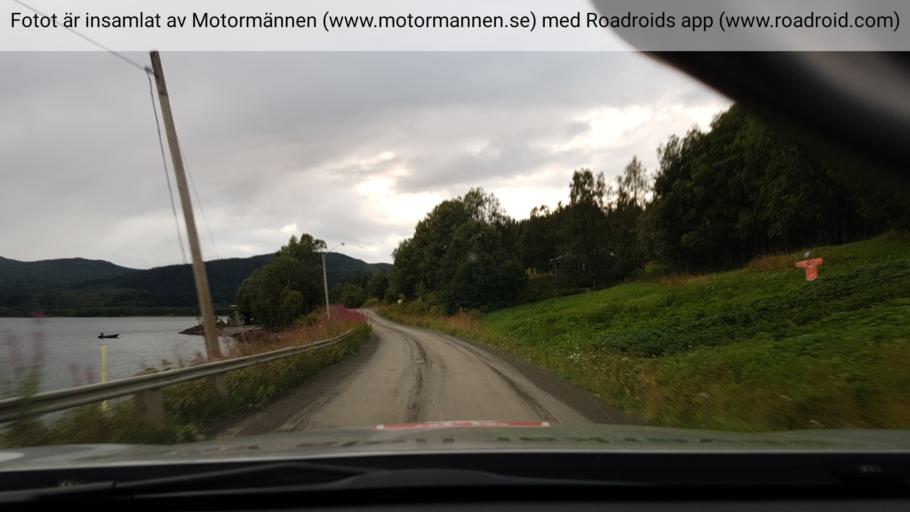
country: NO
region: Nordland
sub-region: Hattfjelldal
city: Hattfjelldal
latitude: 65.6527
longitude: 15.1688
